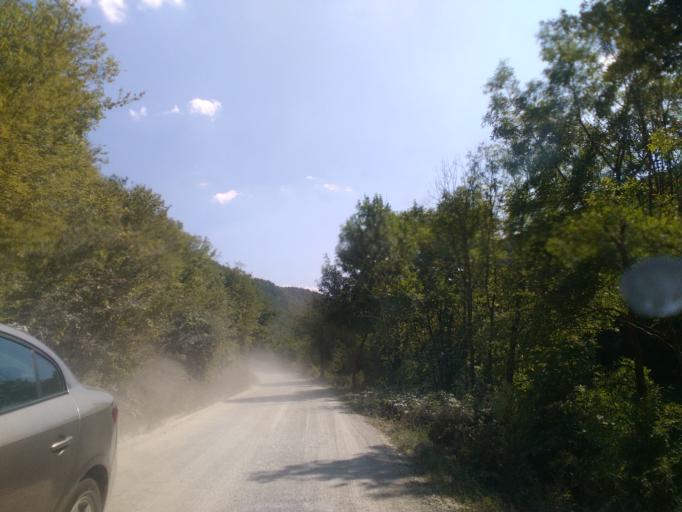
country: BA
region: Federation of Bosnia and Herzegovina
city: Orasac
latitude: 44.6239
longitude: 16.0557
